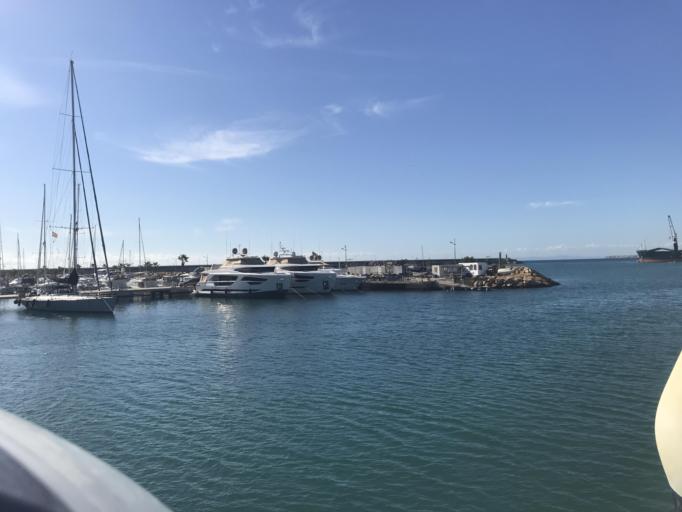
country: ES
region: Valencia
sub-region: Provincia de Alicante
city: Torrevieja
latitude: 37.9719
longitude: -0.6847
